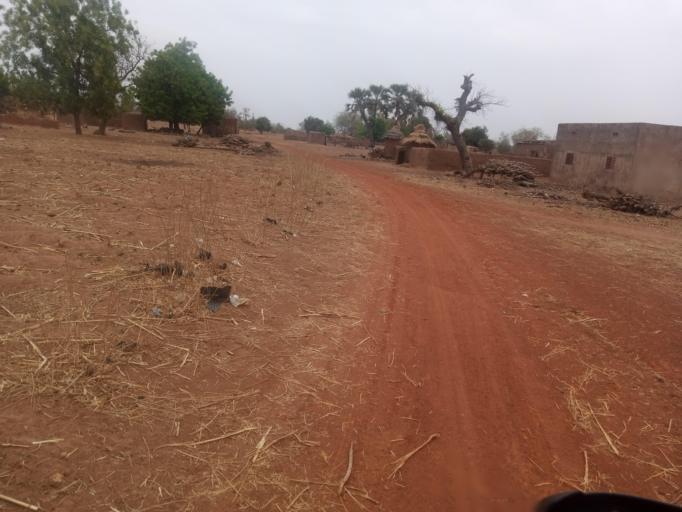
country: BF
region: Boucle du Mouhoun
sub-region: Province de la Kossi
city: Nouna
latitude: 12.8547
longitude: -4.0752
